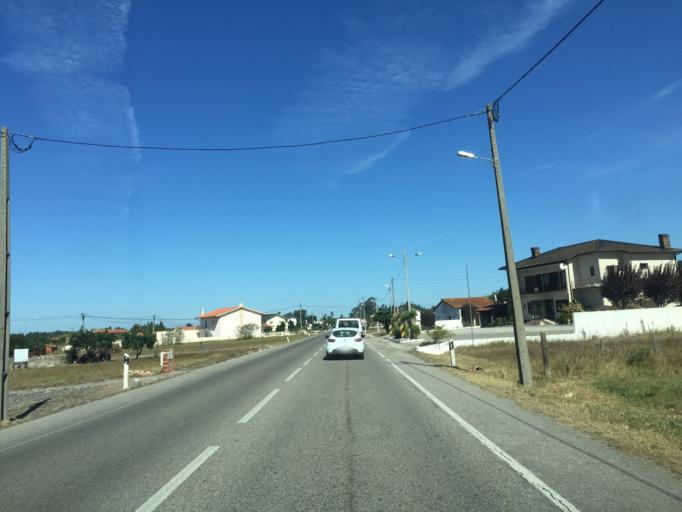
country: PT
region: Coimbra
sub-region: Figueira da Foz
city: Alhadas
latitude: 40.2404
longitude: -8.7925
